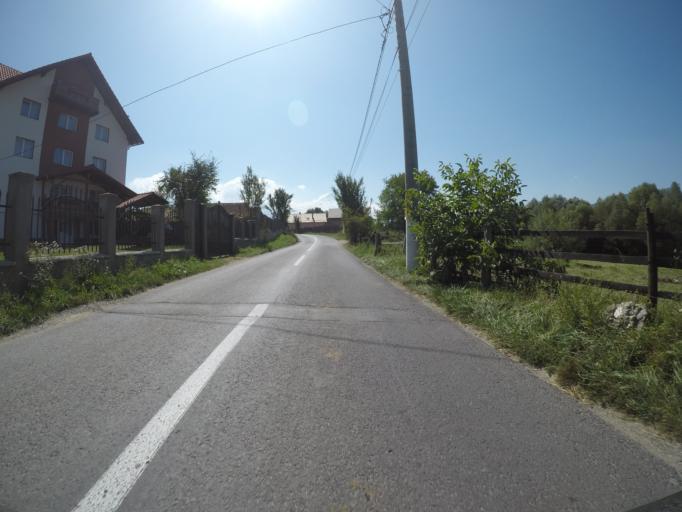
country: RO
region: Brasov
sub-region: Comuna Zarnesti
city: Tohanu Nou
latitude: 45.5467
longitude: 25.3792
